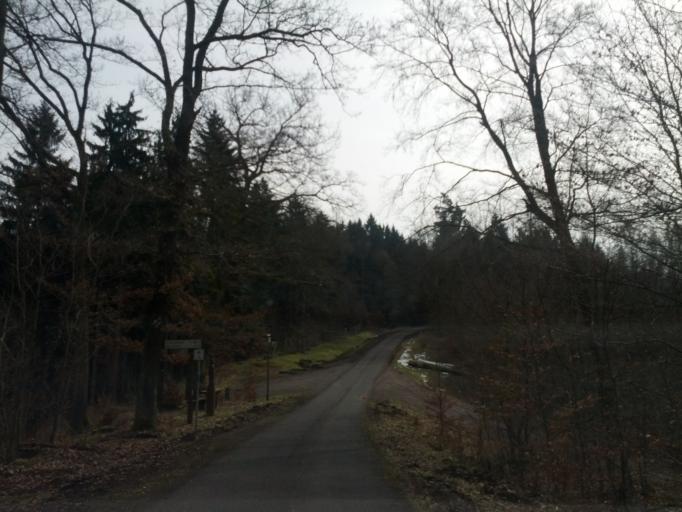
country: DE
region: Thuringia
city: Schweina
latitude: 50.8545
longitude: 10.3160
